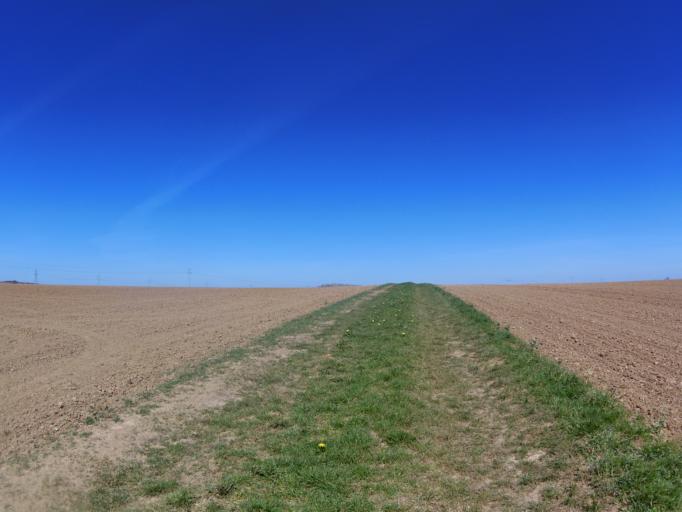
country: DE
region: Bavaria
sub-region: Regierungsbezirk Unterfranken
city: Biebelried
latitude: 49.8037
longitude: 10.1012
